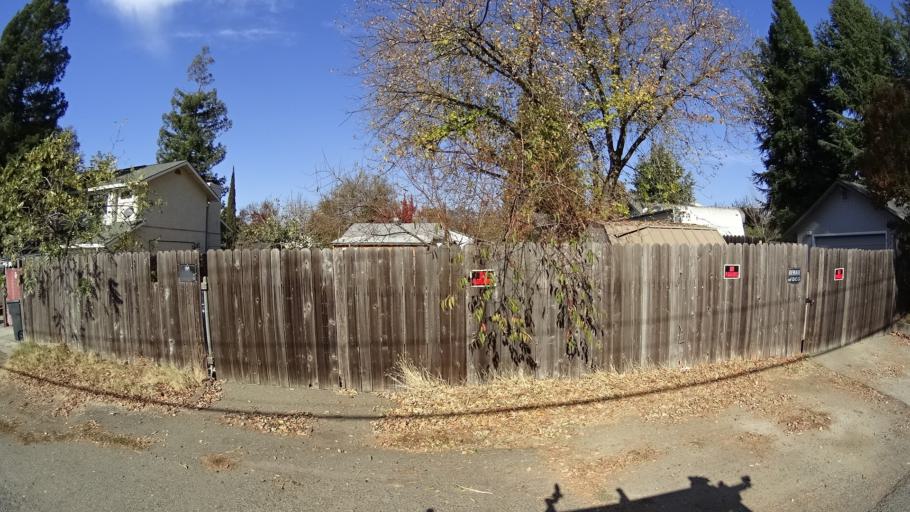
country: US
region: California
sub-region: Sacramento County
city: Fair Oaks
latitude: 38.6701
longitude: -121.2903
